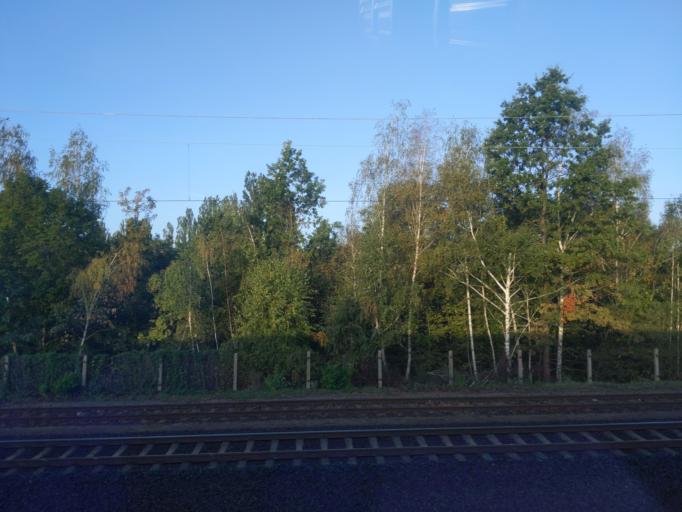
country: DE
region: Saxony
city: Coswig
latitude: 51.1282
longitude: 13.5729
